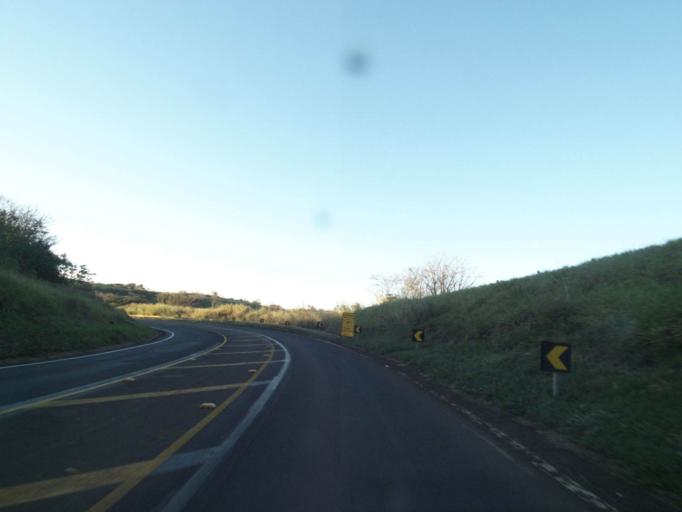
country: BR
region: Parana
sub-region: Apucarana
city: Apucarana
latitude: -23.6706
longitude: -51.1194
